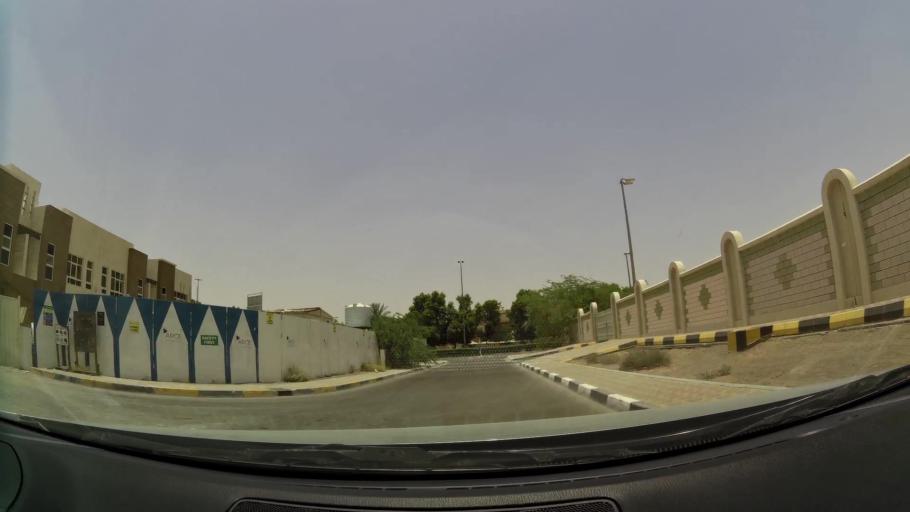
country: AE
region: Abu Dhabi
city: Al Ain
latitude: 24.2205
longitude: 55.7348
